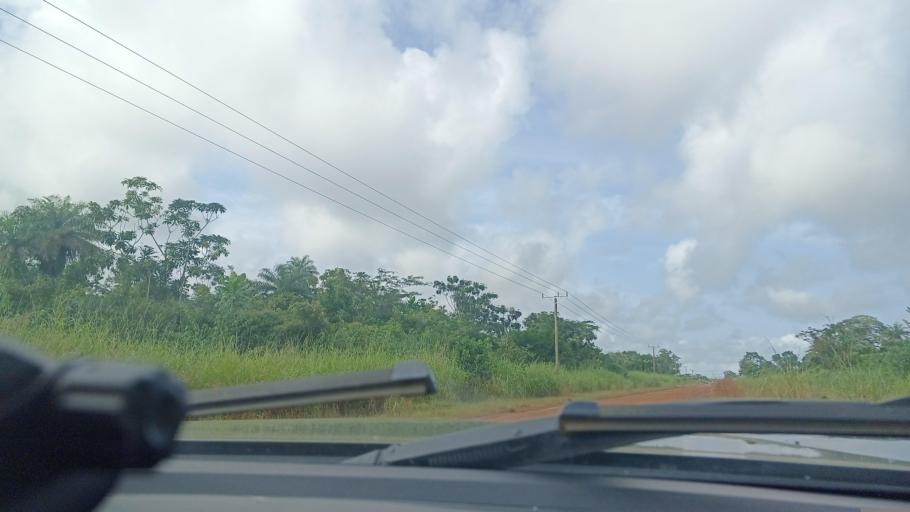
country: LR
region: Grand Cape Mount
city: Robertsport
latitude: 6.6889
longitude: -11.1161
